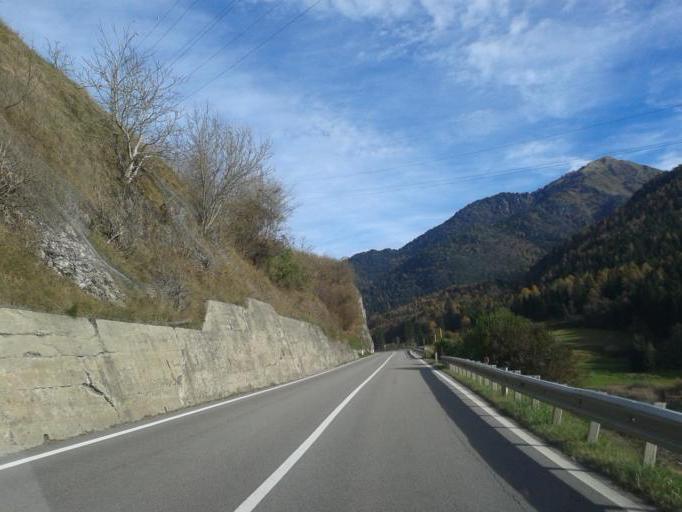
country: IT
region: Trentino-Alto Adige
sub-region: Provincia di Trento
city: Roncone
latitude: 45.9866
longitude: 10.6773
